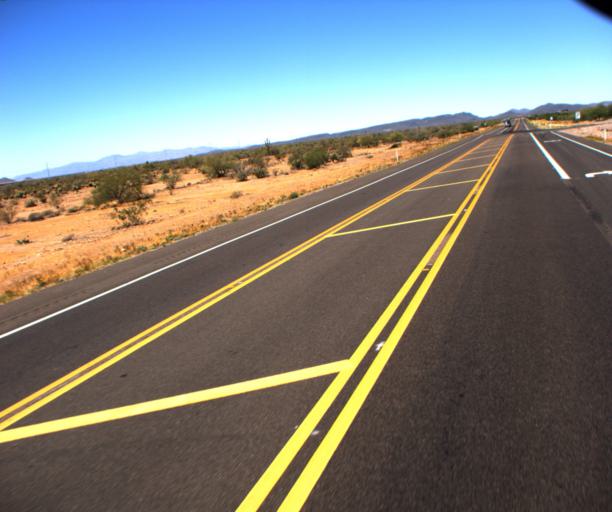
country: US
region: Arizona
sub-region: Maricopa County
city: Anthem
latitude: 33.7978
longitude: -112.2044
